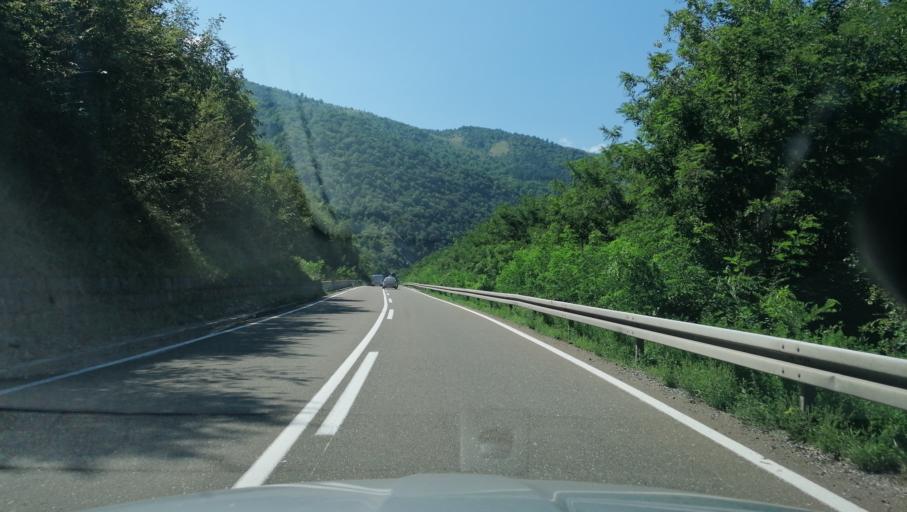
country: RS
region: Central Serbia
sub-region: Raski Okrug
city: Kraljevo
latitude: 43.5957
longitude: 20.5669
